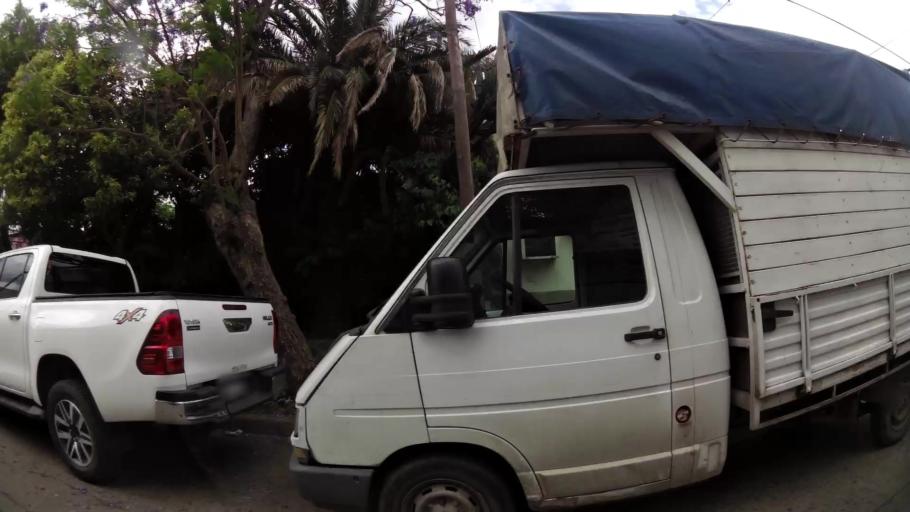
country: AR
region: Santa Fe
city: Gobernador Galvez
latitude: -33.0019
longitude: -60.6504
